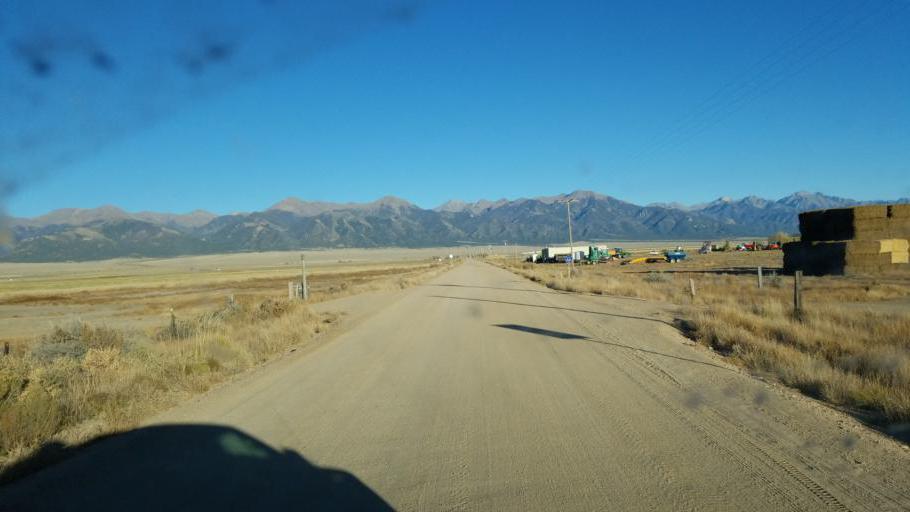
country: US
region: Colorado
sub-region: Saguache County
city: Saguache
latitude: 38.1007
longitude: -105.9193
